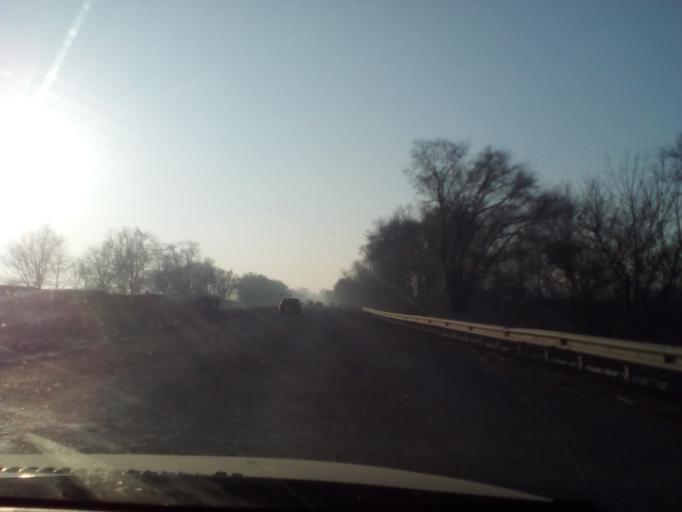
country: KZ
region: Almaty Oblysy
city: Burunday
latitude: 43.2233
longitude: 76.5930
